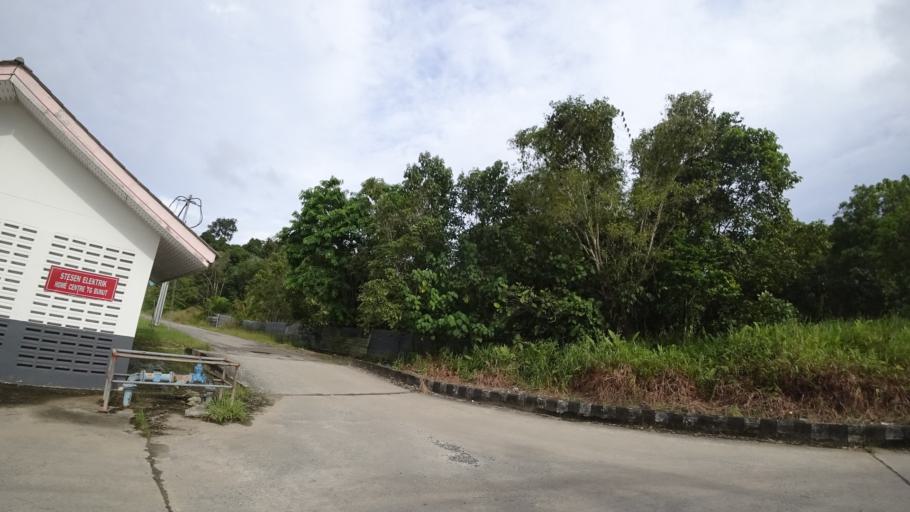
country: BN
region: Brunei and Muara
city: Bandar Seri Begawan
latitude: 4.8895
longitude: 114.8594
